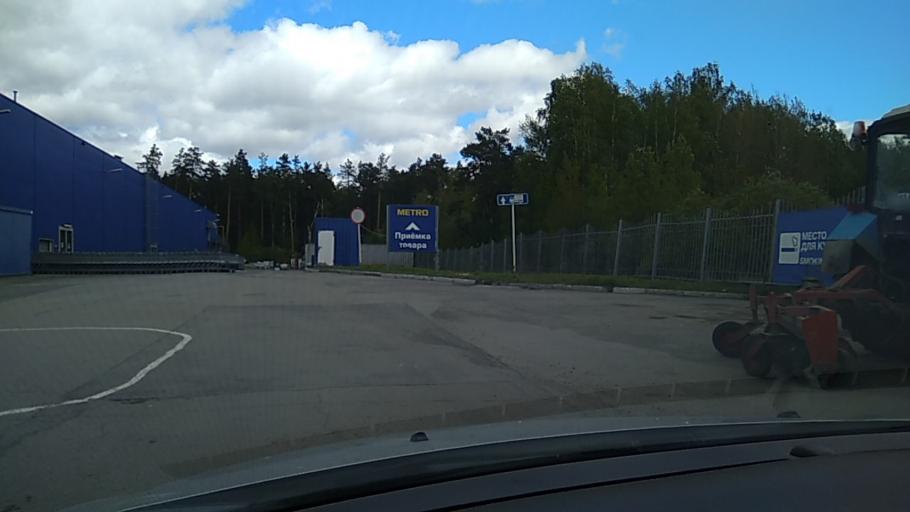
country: RU
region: Sverdlovsk
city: Istok
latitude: 56.8228
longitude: 60.7138
